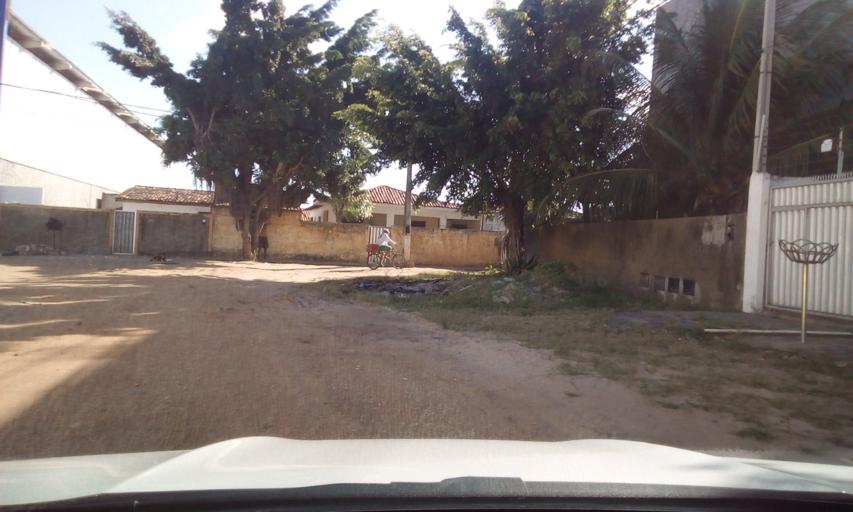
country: BR
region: Paraiba
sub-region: Cabedelo
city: Cabedelo
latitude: -7.0343
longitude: -34.8448
